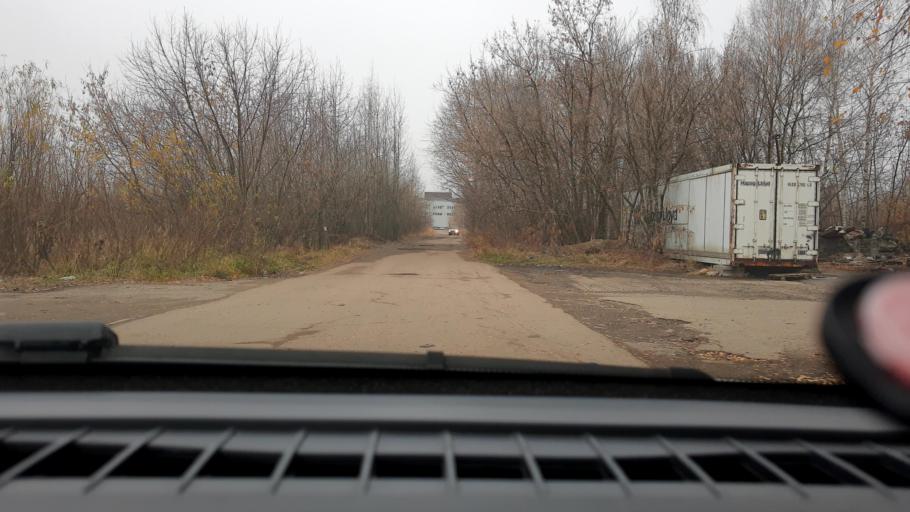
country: RU
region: Nizjnij Novgorod
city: Nizhniy Novgorod
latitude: 56.3332
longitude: 43.9014
